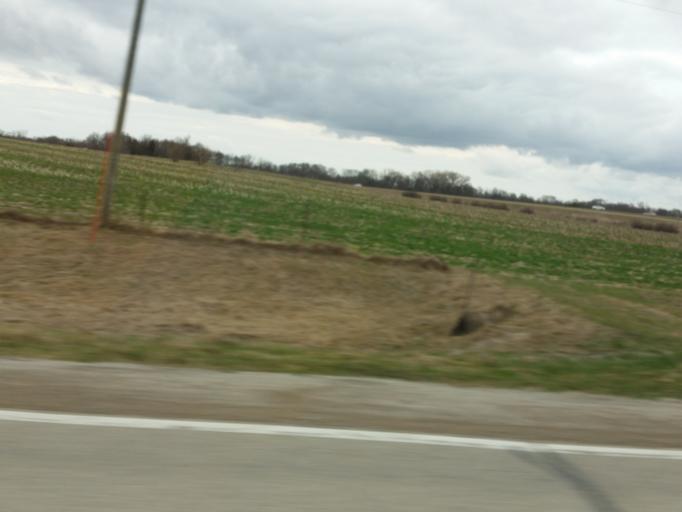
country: US
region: Iowa
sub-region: Benton County
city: Urbana
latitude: 42.3120
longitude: -91.9827
